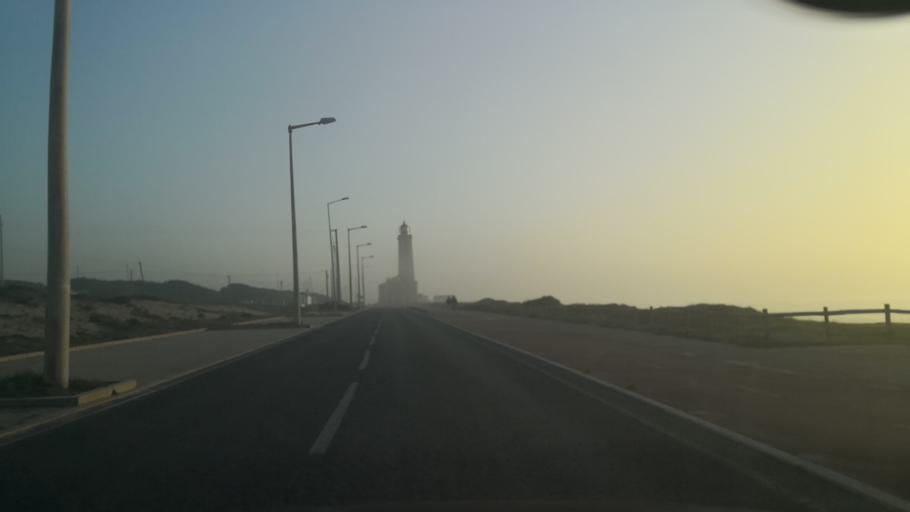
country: PT
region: Leiria
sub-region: Marinha Grande
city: Marinha Grande
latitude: 39.7664
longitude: -9.0299
